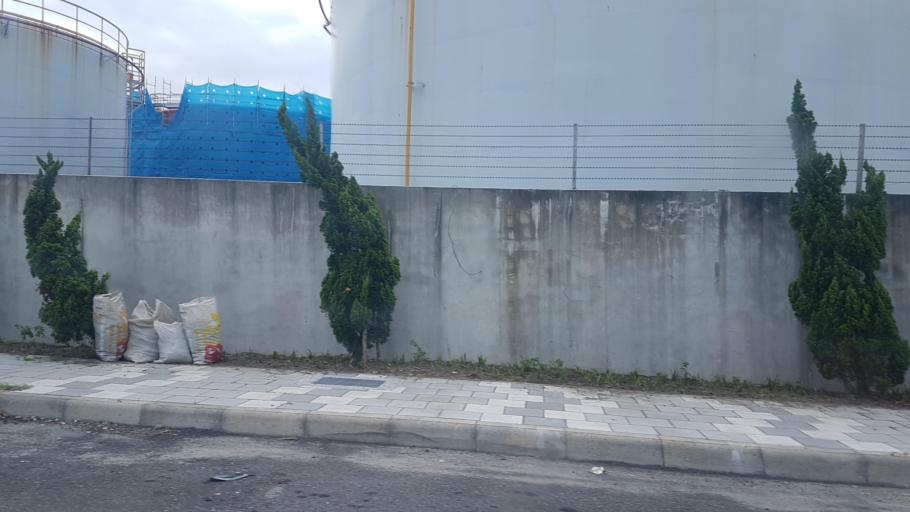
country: TW
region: Taiwan
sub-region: Hualien
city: Hualian
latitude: 23.9988
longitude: 121.6328
